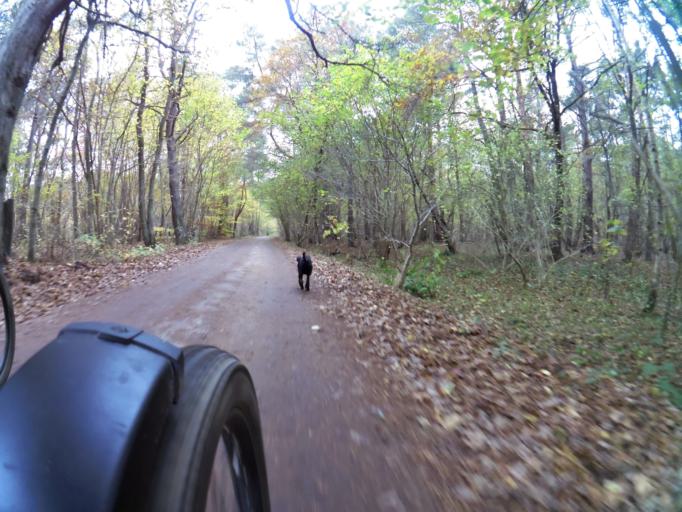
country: PL
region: Pomeranian Voivodeship
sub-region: Powiat pucki
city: Krokowa
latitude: 54.8285
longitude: 18.1020
